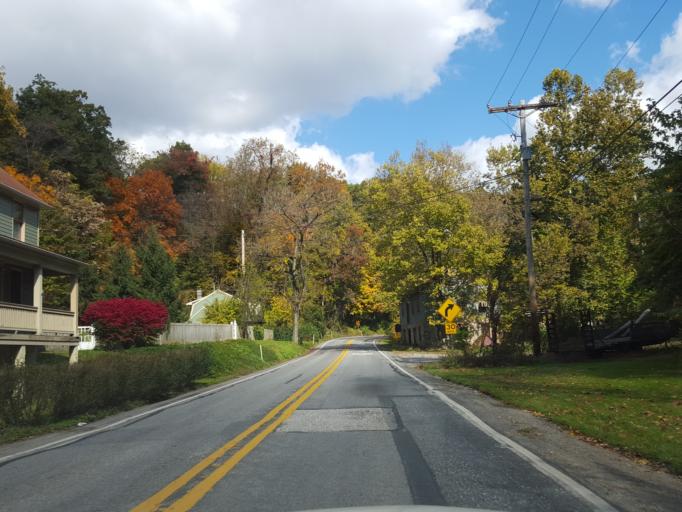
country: US
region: Pennsylvania
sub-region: York County
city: Valley View
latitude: 39.9467
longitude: -76.6703
